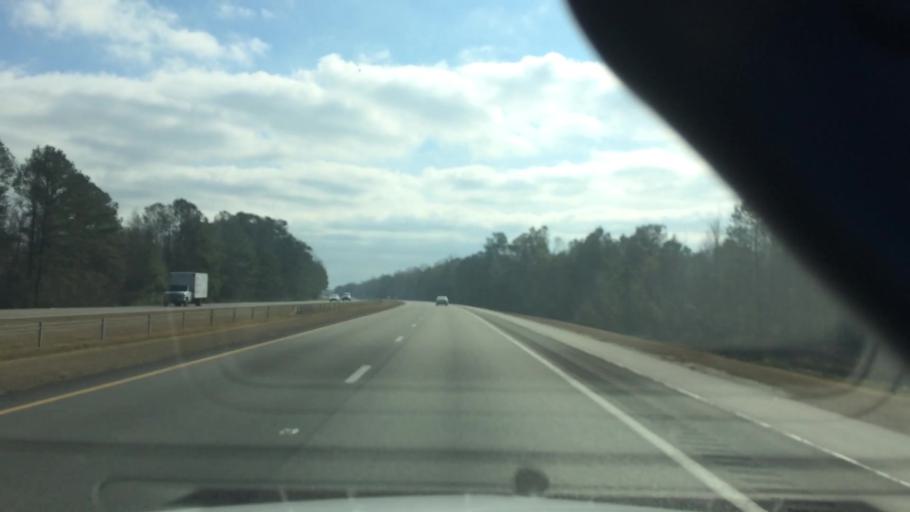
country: US
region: North Carolina
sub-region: Pender County
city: Rocky Point
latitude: 34.4634
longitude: -77.8802
